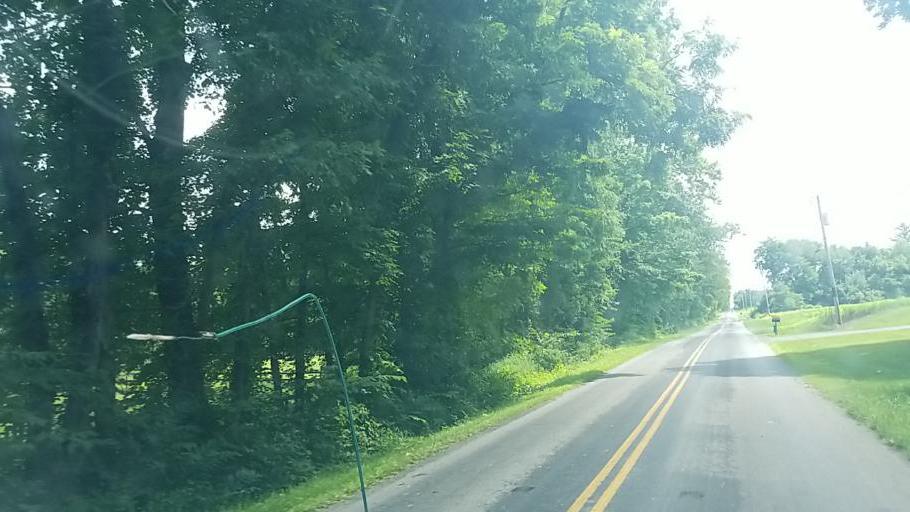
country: US
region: Ohio
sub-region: Wayne County
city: West Salem
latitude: 41.0142
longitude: -82.0738
